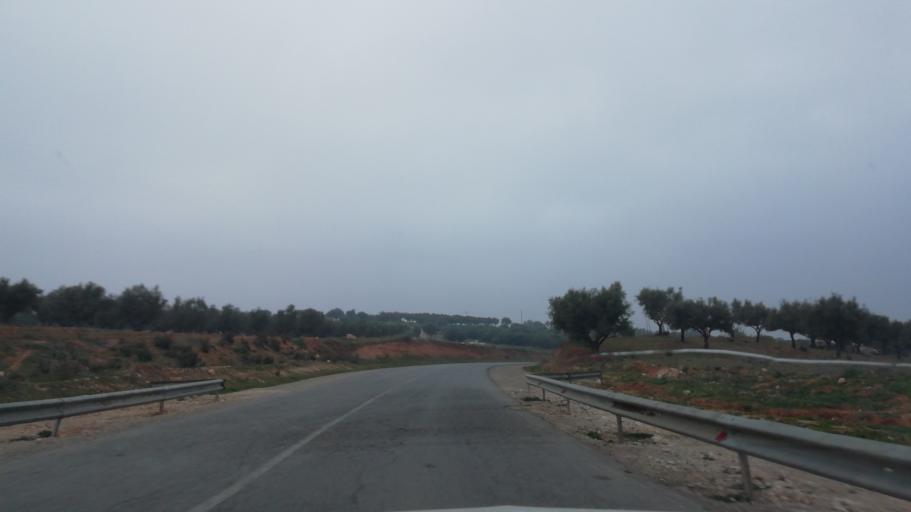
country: DZ
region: Mascara
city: Mascara
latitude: 35.3880
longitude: 0.1620
